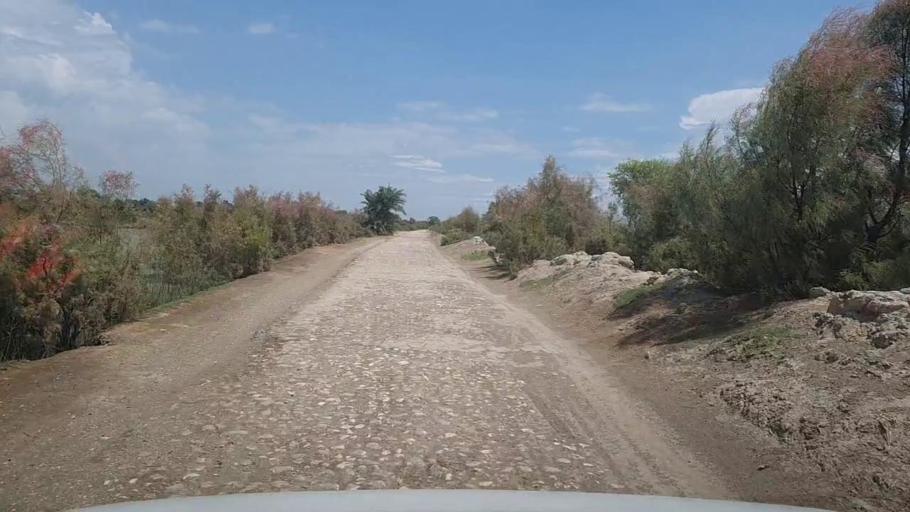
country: PK
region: Sindh
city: Kandhkot
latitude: 28.3419
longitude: 69.2340
